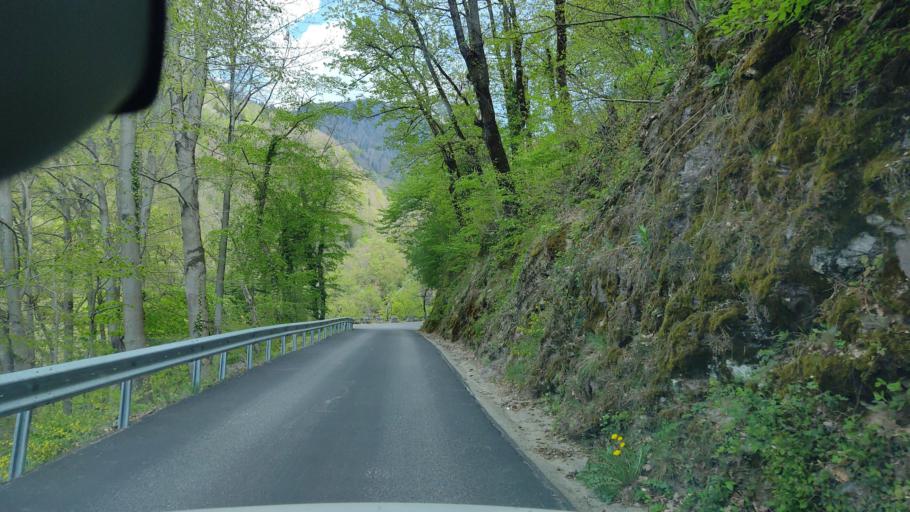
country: FR
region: Rhone-Alpes
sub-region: Departement de la Savoie
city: Ugine
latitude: 45.7503
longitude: 6.4354
